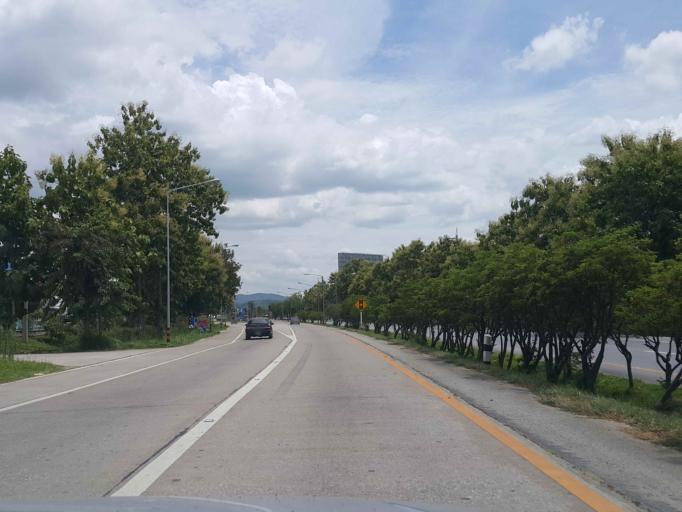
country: TH
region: Lamphun
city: Lamphun
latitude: 18.5561
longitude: 99.0465
